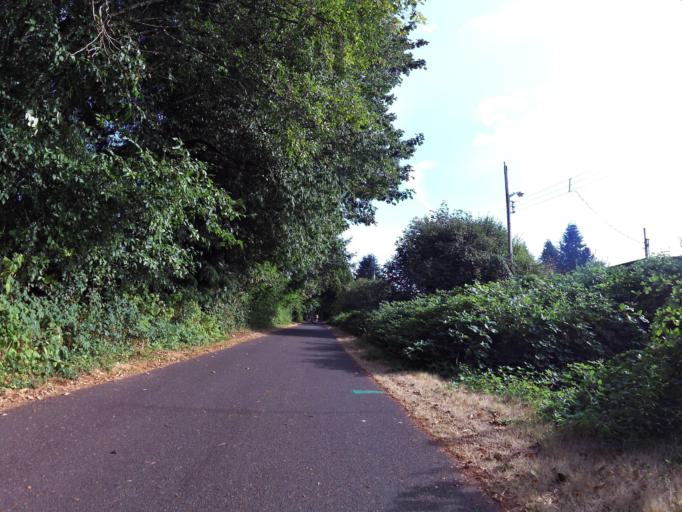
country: US
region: Washington
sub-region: Thurston County
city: Lacey
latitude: 47.0299
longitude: -122.8374
